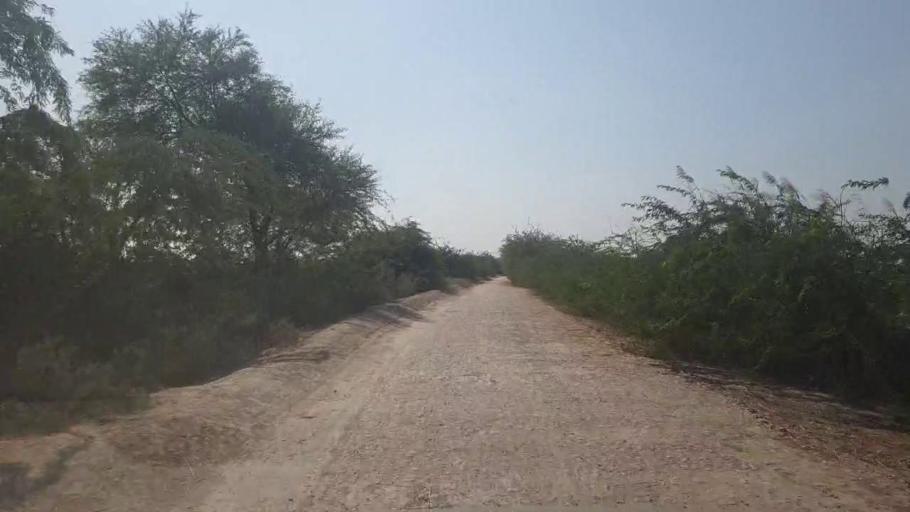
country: PK
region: Sindh
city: Badin
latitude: 24.6538
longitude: 68.9185
